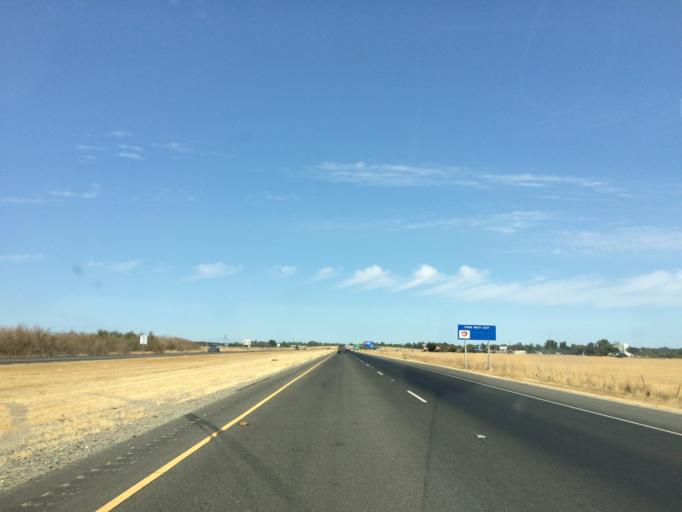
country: US
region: California
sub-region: Yolo County
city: Dunnigan
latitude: 38.8734
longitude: -121.9661
